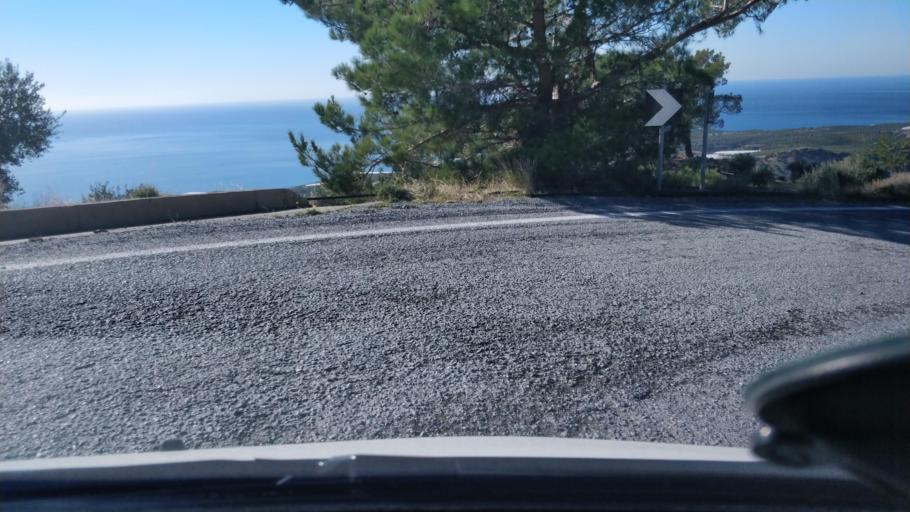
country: GR
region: Crete
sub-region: Nomos Irakleiou
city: Arkalochori
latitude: 35.0055
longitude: 25.4379
